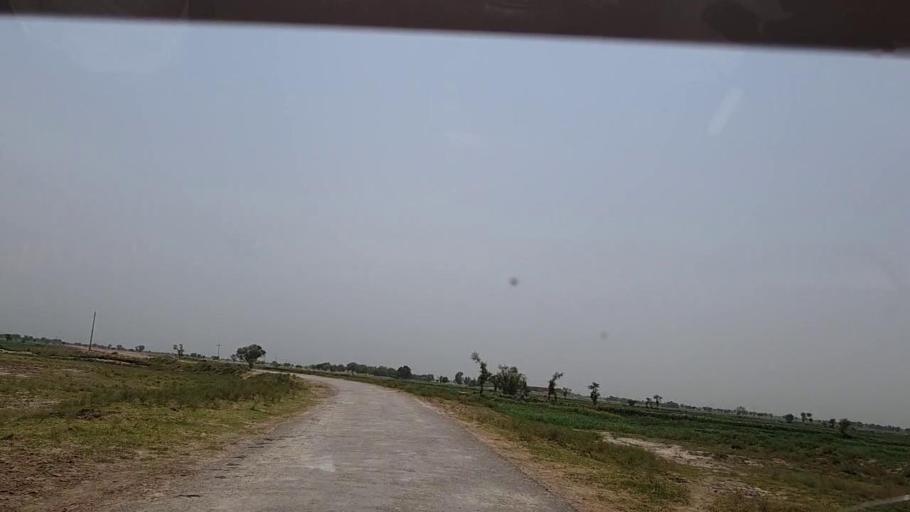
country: PK
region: Sindh
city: Khairpur Nathan Shah
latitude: 27.0165
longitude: 67.6569
